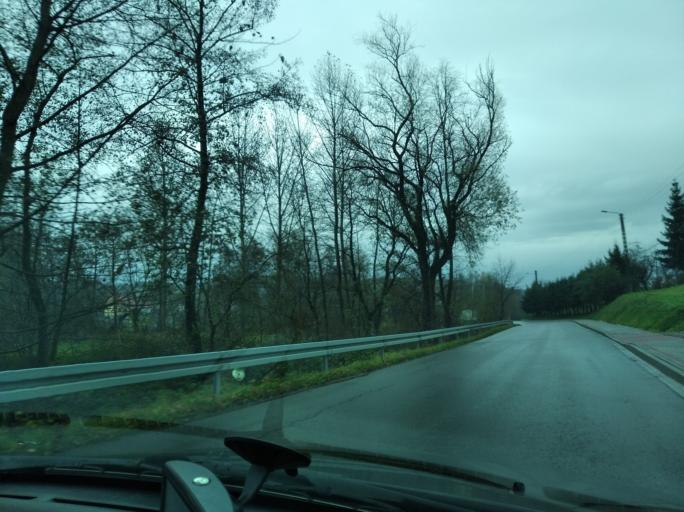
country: PL
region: Subcarpathian Voivodeship
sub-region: Powiat rzeszowski
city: Lubenia
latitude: 49.9199
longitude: 21.9551
